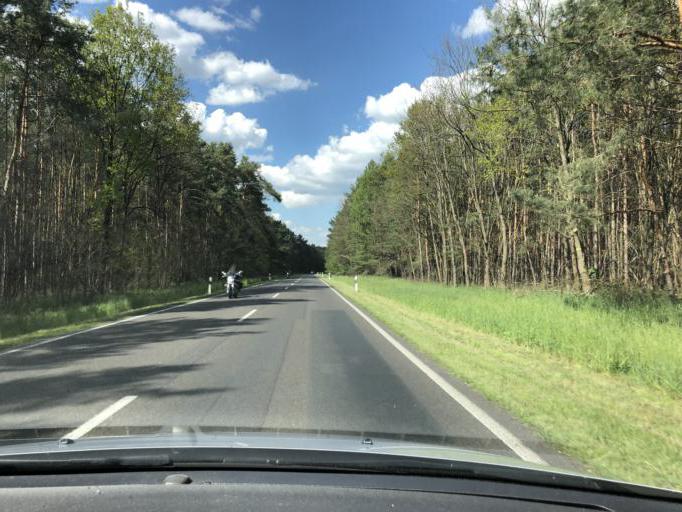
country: DE
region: Brandenburg
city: Storkow
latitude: 52.3004
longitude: 13.9028
